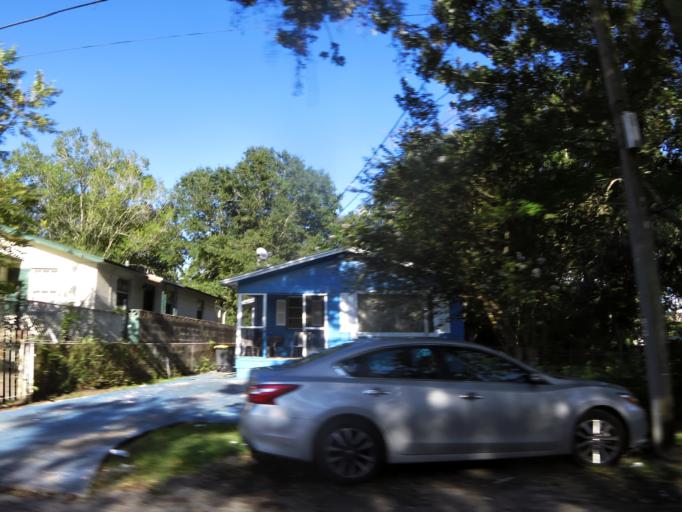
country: US
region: Florida
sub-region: Duval County
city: Jacksonville
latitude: 30.3482
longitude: -81.6898
